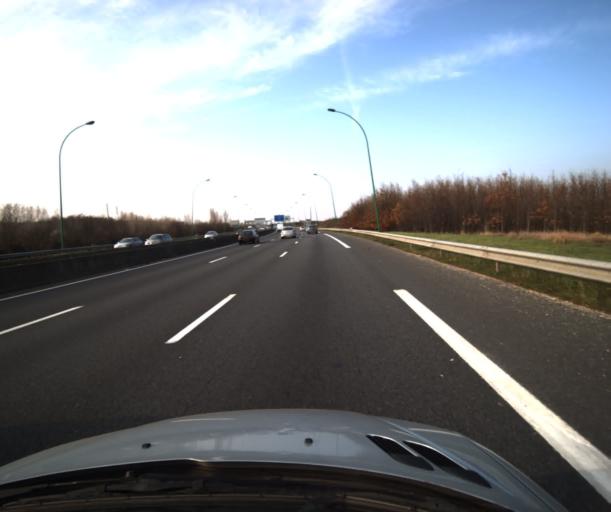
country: FR
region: Midi-Pyrenees
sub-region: Departement de la Haute-Garonne
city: Balma
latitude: 43.5809
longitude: 1.4983
